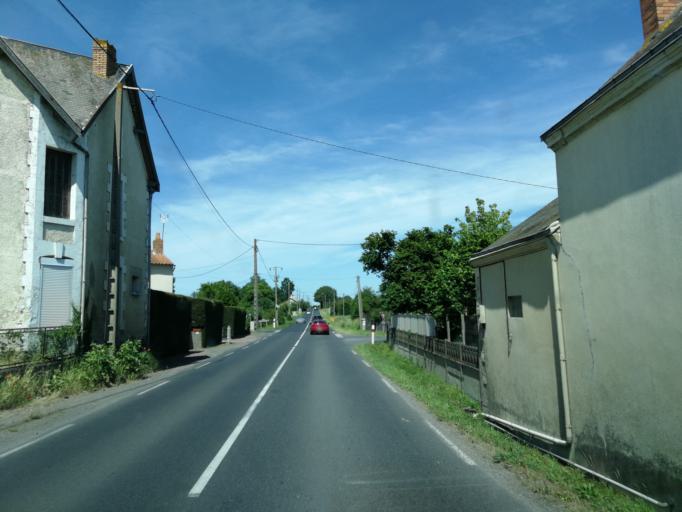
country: FR
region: Poitou-Charentes
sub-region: Departement des Deux-Sevres
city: Saint-Jean-de-Thouars
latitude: 46.9472
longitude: -0.2305
